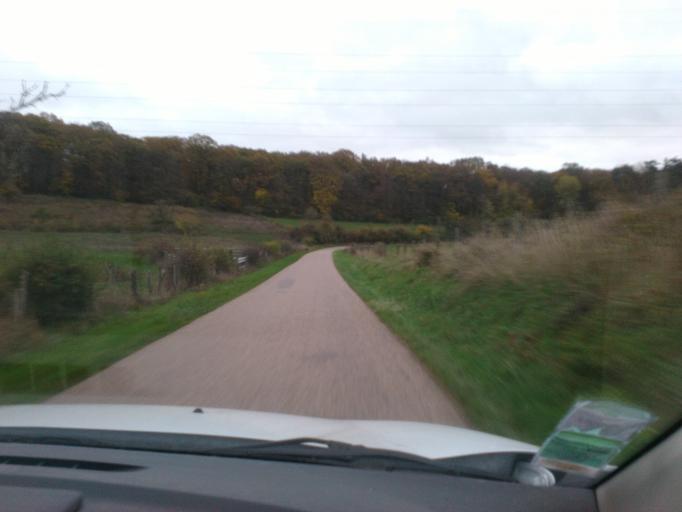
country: FR
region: Lorraine
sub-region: Departement des Vosges
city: Mirecourt
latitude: 48.3030
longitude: 6.2140
